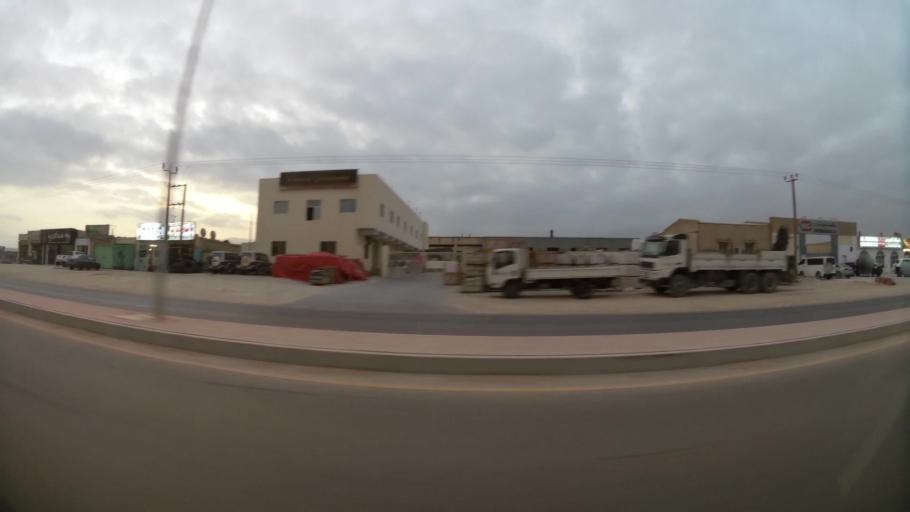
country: OM
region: Zufar
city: Salalah
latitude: 17.0281
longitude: 54.0488
